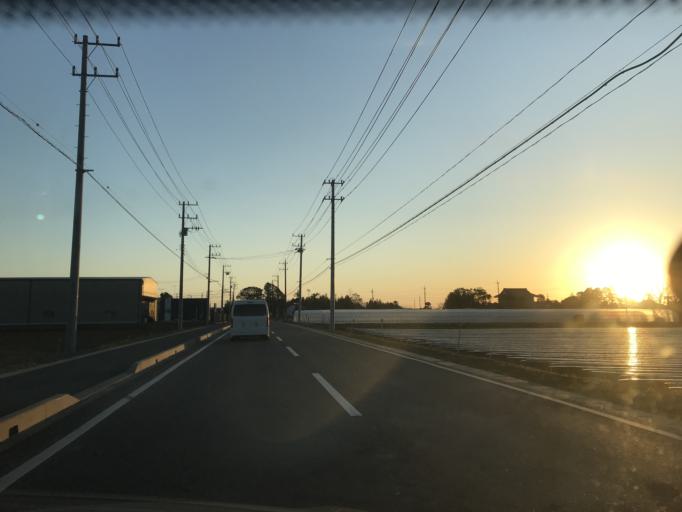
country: JP
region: Chiba
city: Sawara
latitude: 35.8353
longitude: 140.5386
